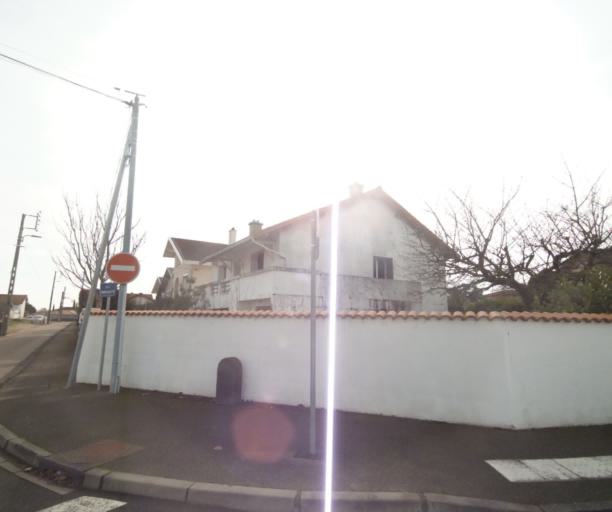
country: FR
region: Rhone-Alpes
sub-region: Departement de la Loire
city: Riorges
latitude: 46.0224
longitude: 4.0491
